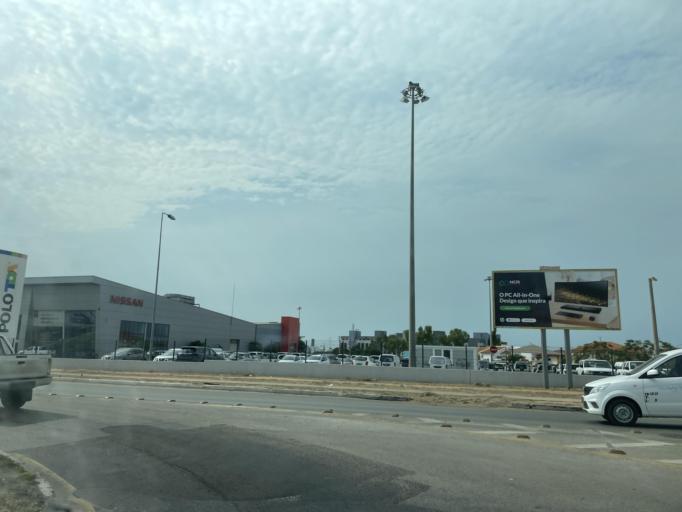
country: AO
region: Luanda
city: Luanda
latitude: -8.9127
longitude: 13.1977
